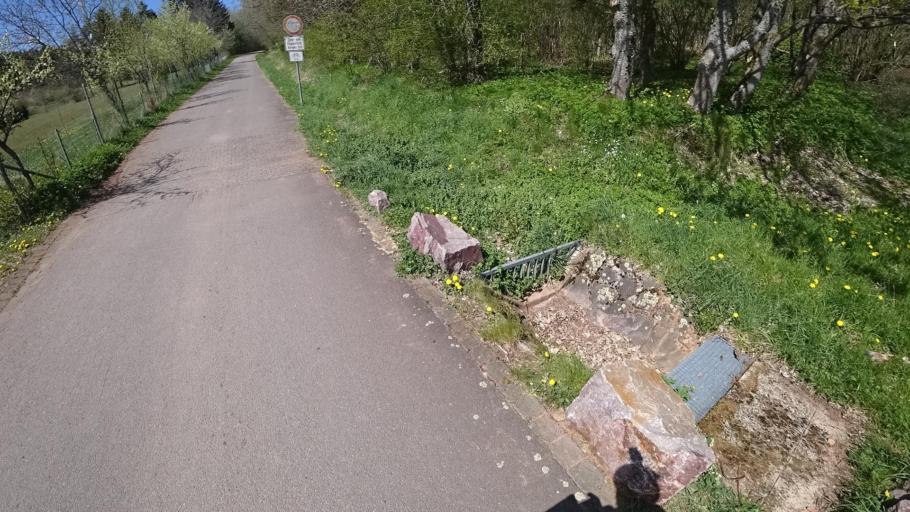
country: DE
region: Rheinland-Pfalz
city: Gusenburg
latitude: 49.6383
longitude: 6.8934
